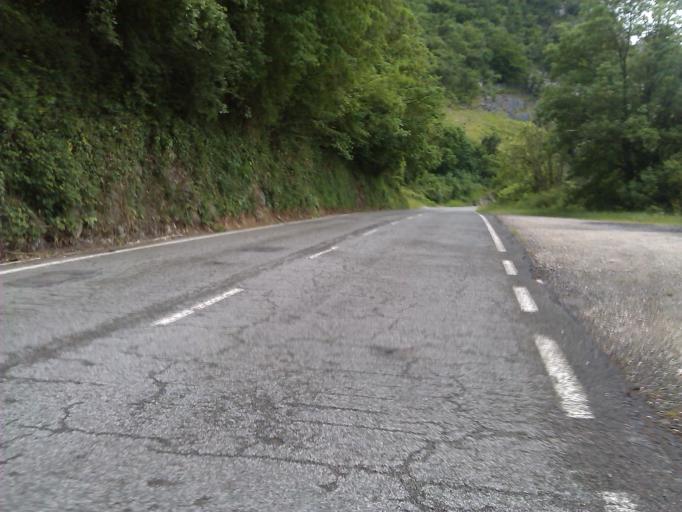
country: ES
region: Navarre
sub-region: Provincia de Navarra
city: Irurtzun
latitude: 42.9414
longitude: -1.8233
